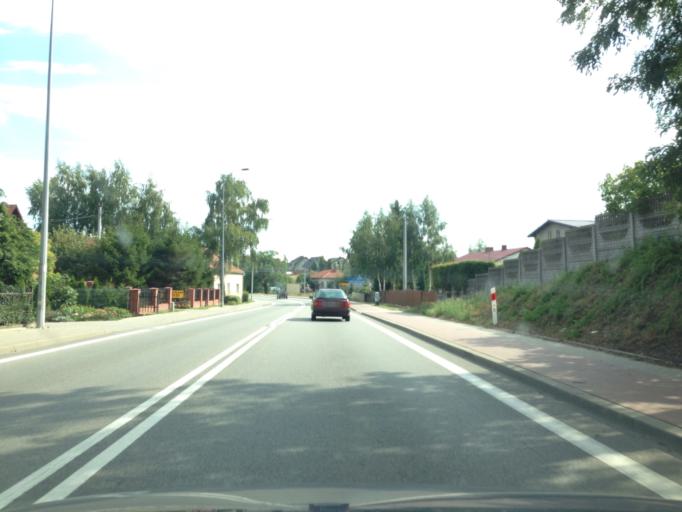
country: PL
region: Pomeranian Voivodeship
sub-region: Powiat gdanski
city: Pszczolki
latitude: 54.1832
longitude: 18.6794
